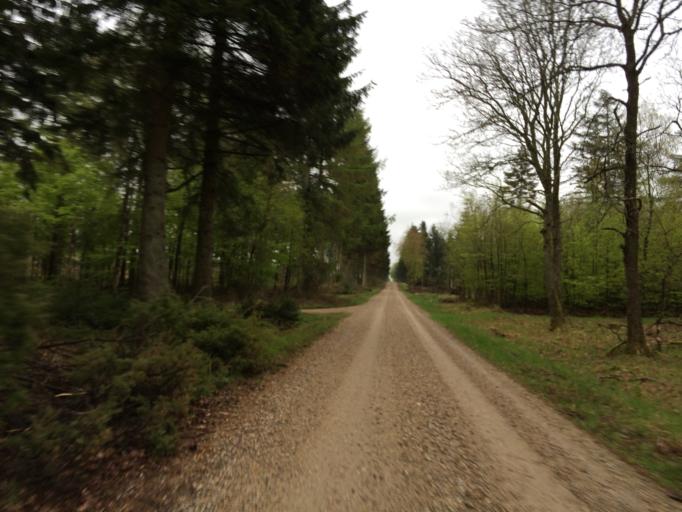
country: DK
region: Central Jutland
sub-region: Holstebro Kommune
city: Ulfborg
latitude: 56.2613
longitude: 8.4412
